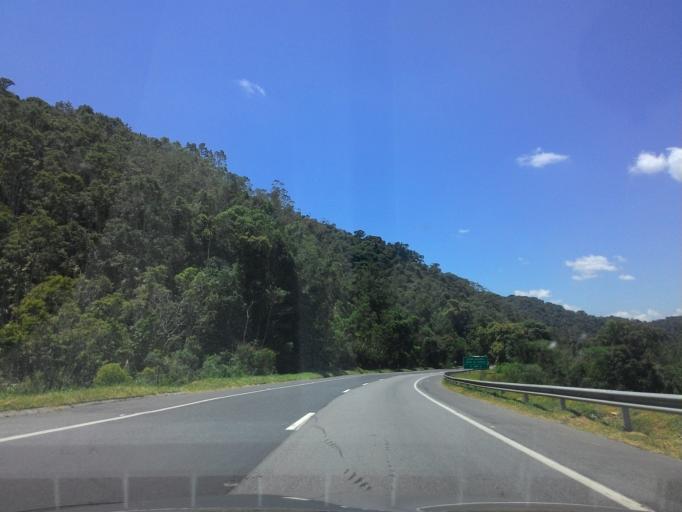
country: BR
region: Sao Paulo
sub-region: Cajati
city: Cajati
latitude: -24.9635
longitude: -48.4240
